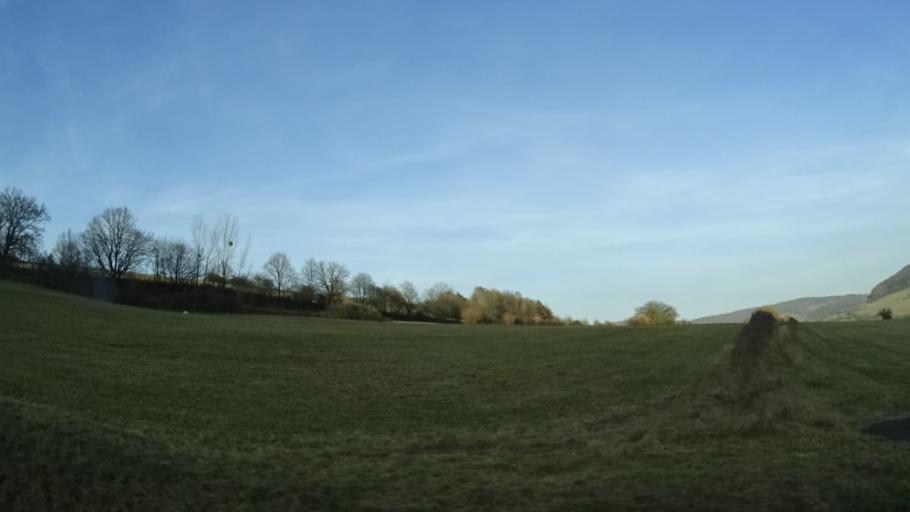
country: DE
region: Bavaria
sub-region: Regierungsbezirk Unterfranken
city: Zeitlofs
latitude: 50.3021
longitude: 9.6476
